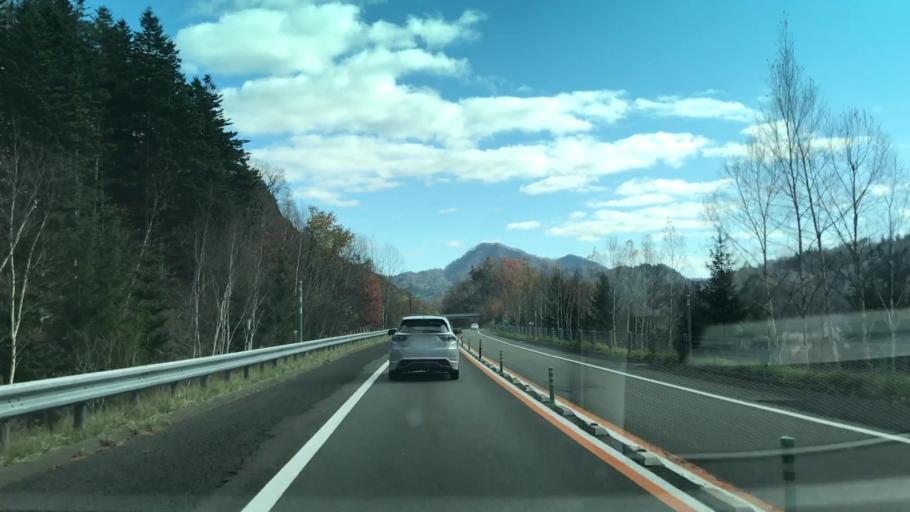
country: JP
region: Hokkaido
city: Chitose
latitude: 42.9119
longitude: 141.9778
